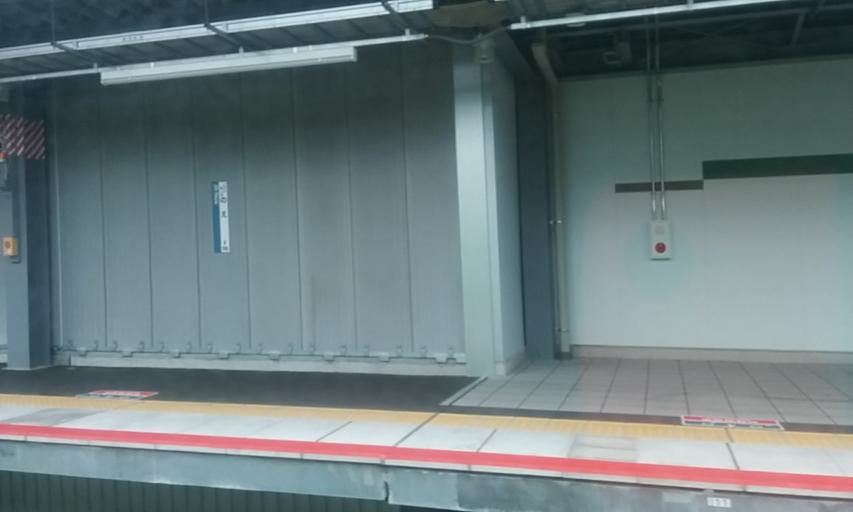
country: JP
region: Osaka
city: Moriguchi
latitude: 34.7068
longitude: 135.5414
